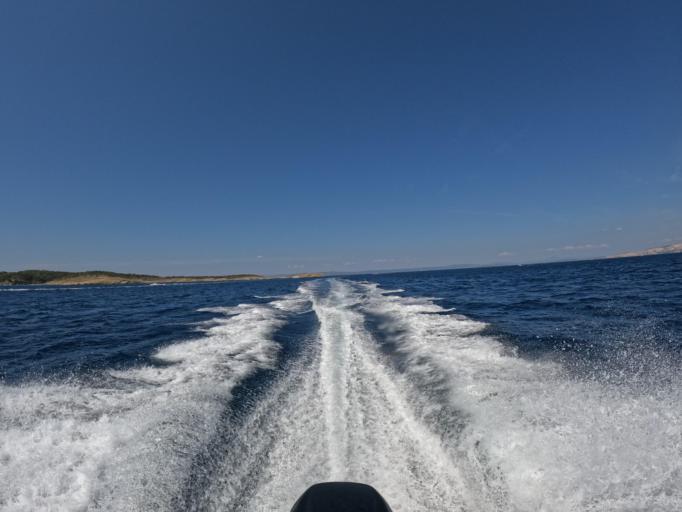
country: HR
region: Primorsko-Goranska
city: Lopar
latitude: 44.8529
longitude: 14.7411
